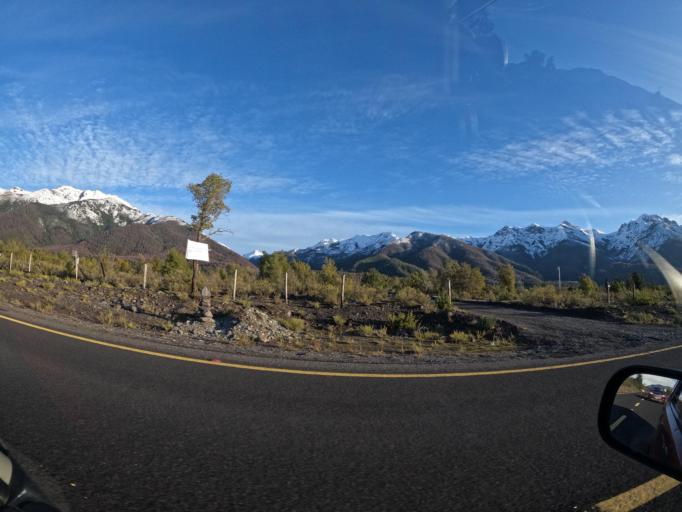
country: CL
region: Biobio
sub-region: Provincia de Nuble
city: Coihueco
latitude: -37.3504
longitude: -71.5590
